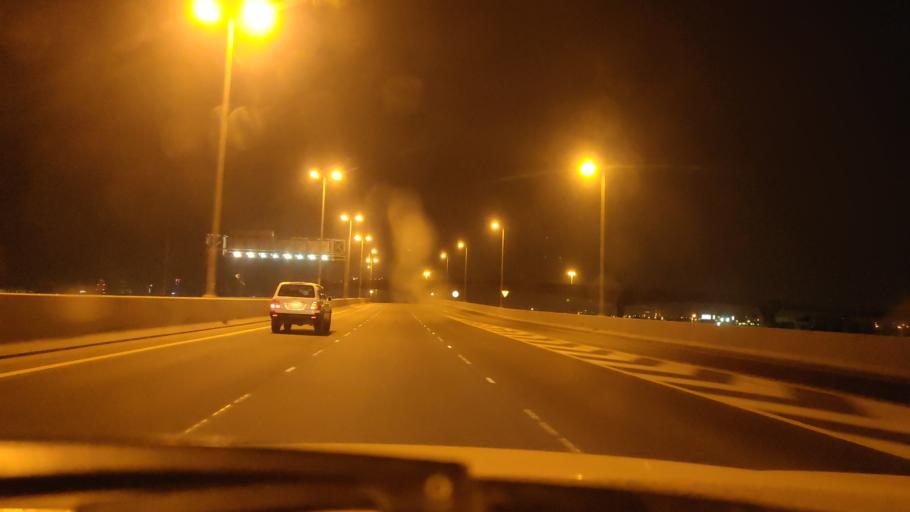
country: KW
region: Al Asimah
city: Ar Rabiyah
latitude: 29.3303
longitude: 47.9279
